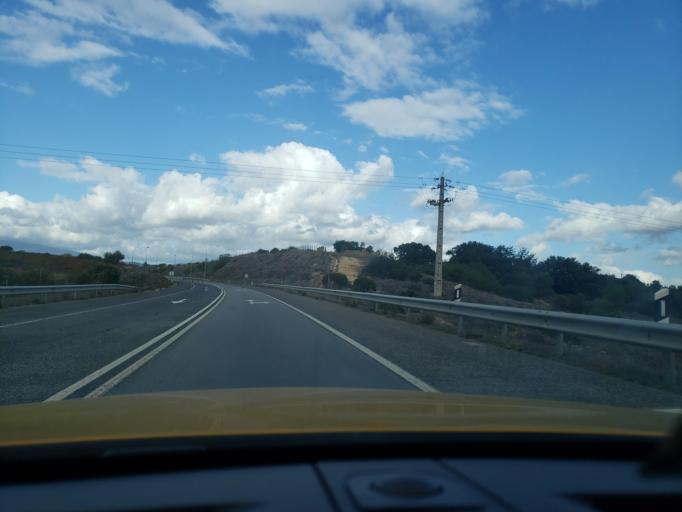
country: PT
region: Faro
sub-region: Portimao
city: Portimao
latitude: 37.1707
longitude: -8.5675
